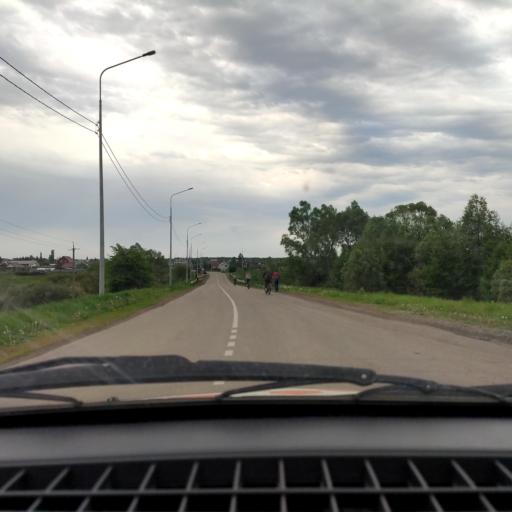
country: RU
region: Bashkortostan
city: Avdon
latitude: 54.5505
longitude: 55.7566
